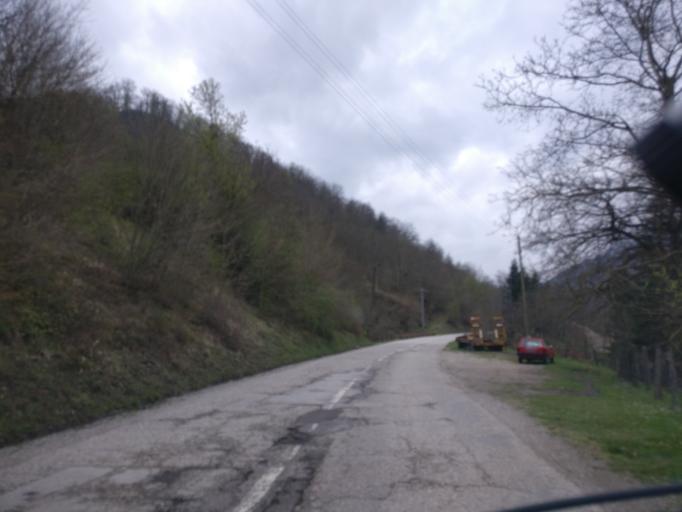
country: BA
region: Republika Srpska
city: Foca
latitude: 43.4510
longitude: 18.7553
